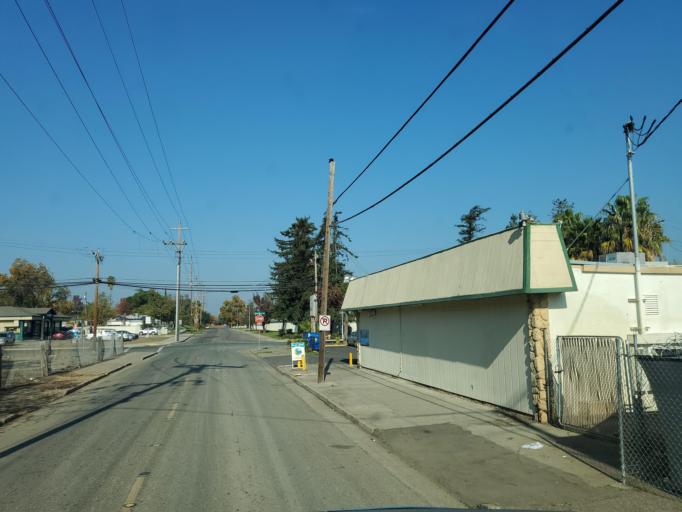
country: US
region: California
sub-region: San Joaquin County
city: Country Club
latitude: 37.9560
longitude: -121.3331
